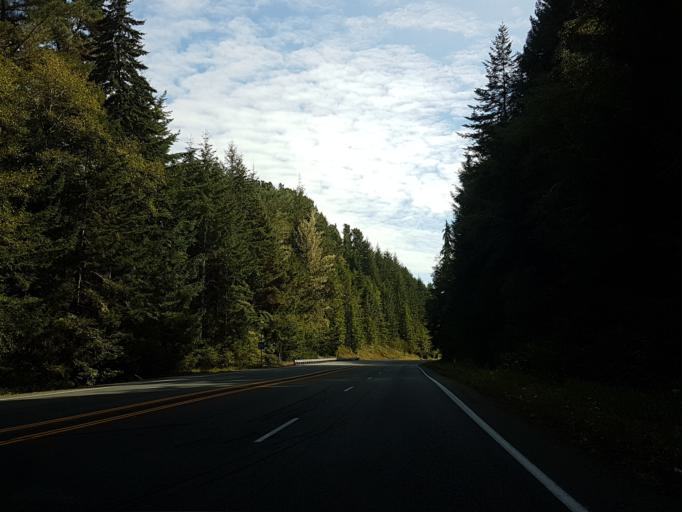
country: US
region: California
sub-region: Del Norte County
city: Bertsch-Oceanview
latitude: 41.4760
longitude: -124.0459
